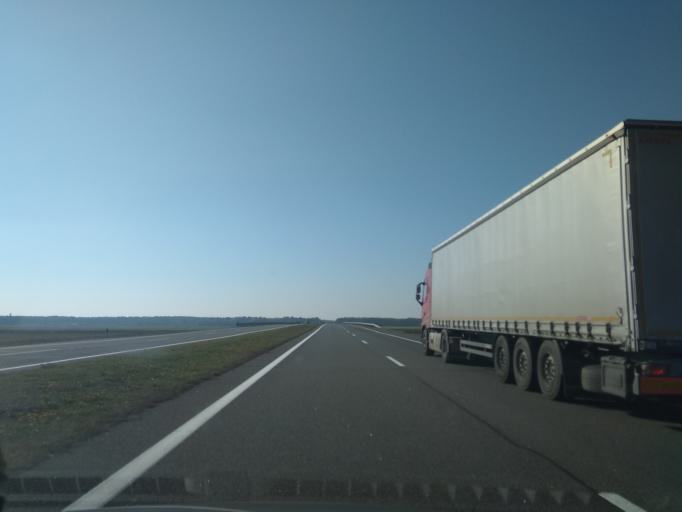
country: BY
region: Brest
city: Ivatsevichy
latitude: 52.7302
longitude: 25.4525
